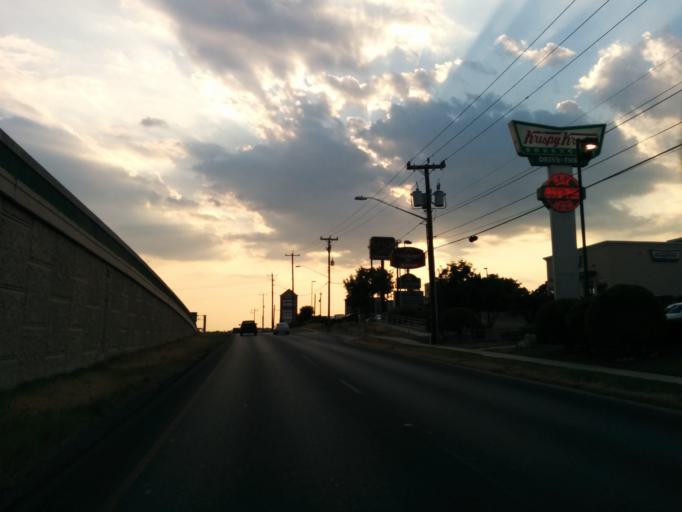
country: US
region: Texas
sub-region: Bexar County
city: Hollywood Park
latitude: 29.6106
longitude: -98.4764
